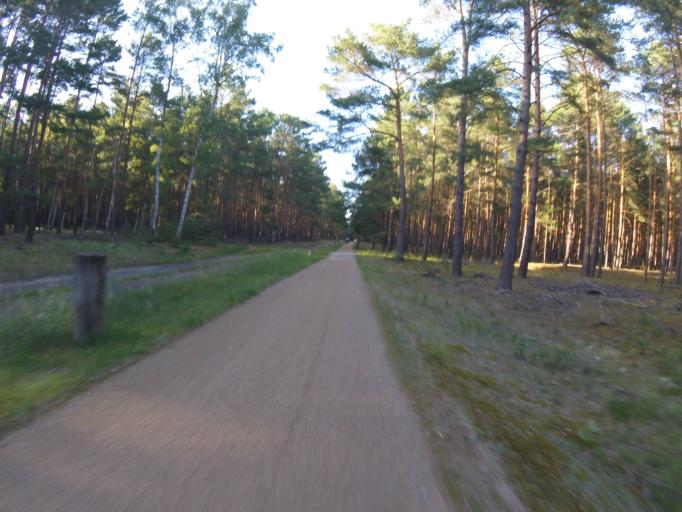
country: DE
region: Brandenburg
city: Munchehofe
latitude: 52.2067
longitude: 13.7693
